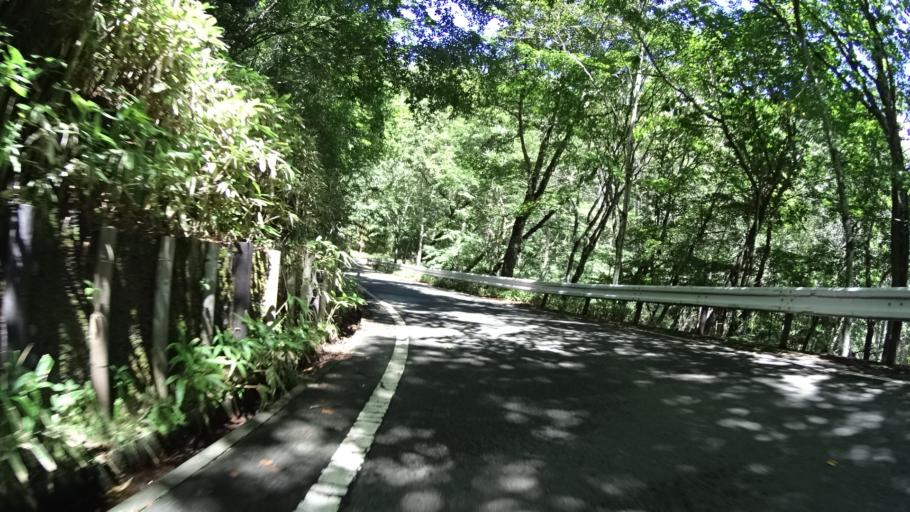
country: JP
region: Yamanashi
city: Enzan
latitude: 35.7323
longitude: 138.8344
